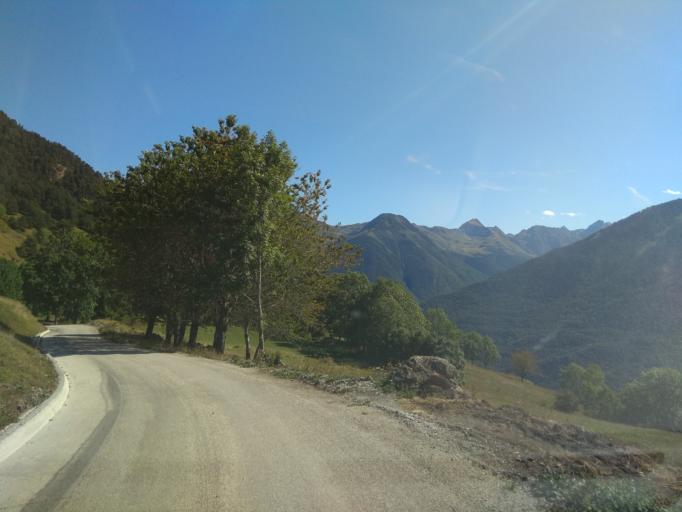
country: ES
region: Catalonia
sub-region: Provincia de Lleida
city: Les
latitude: 42.7606
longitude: 0.7096
